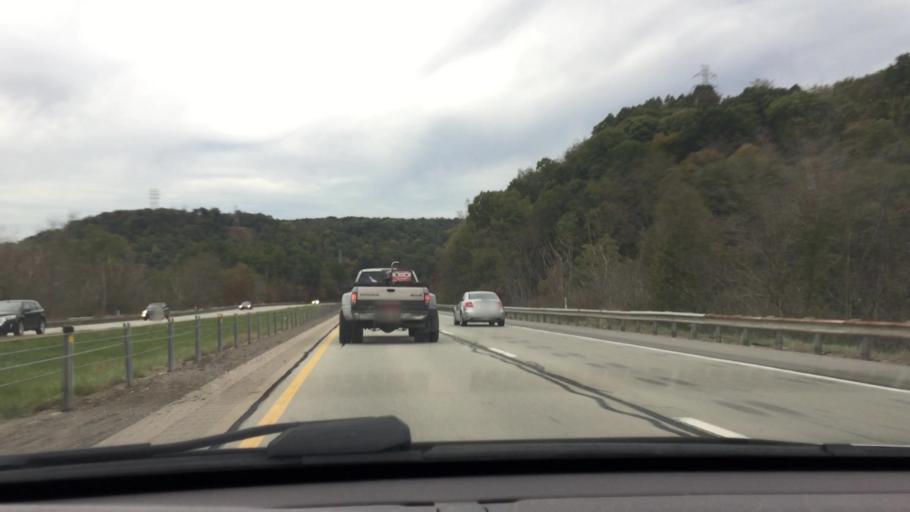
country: US
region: Pennsylvania
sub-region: Beaver County
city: Ambridge
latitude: 40.5738
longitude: -80.2854
